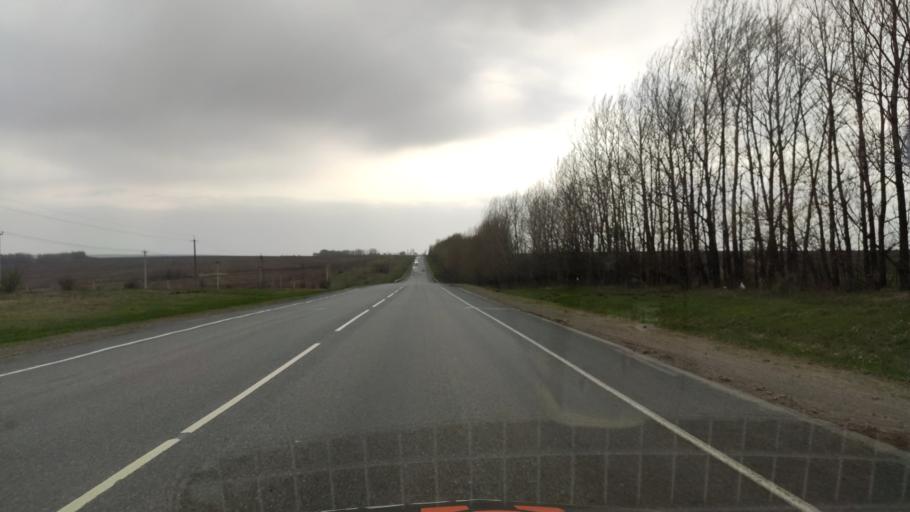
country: RU
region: Kursk
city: Gorshechnoye
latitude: 51.5026
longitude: 37.9878
